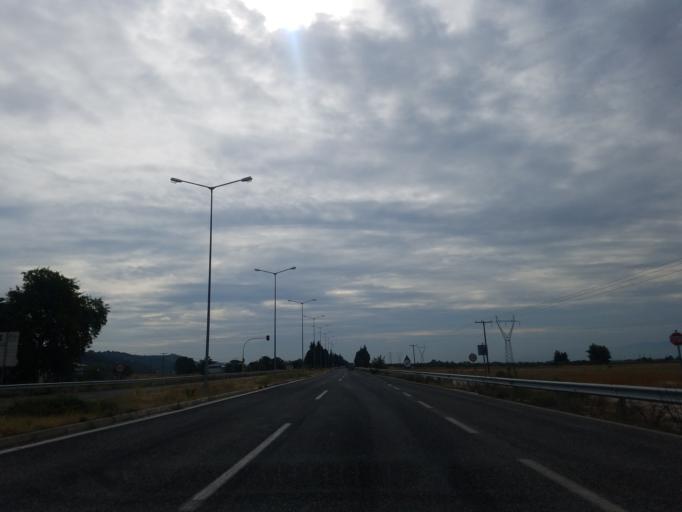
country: GR
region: Thessaly
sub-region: Trikala
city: Vasiliki
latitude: 39.6539
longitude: 21.6811
